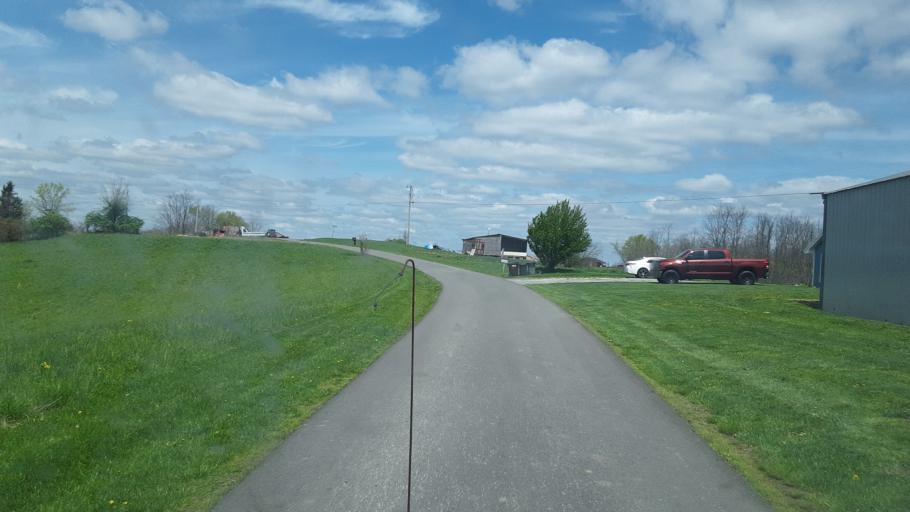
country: US
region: Kentucky
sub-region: Owen County
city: Owenton
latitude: 38.6719
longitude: -84.7835
